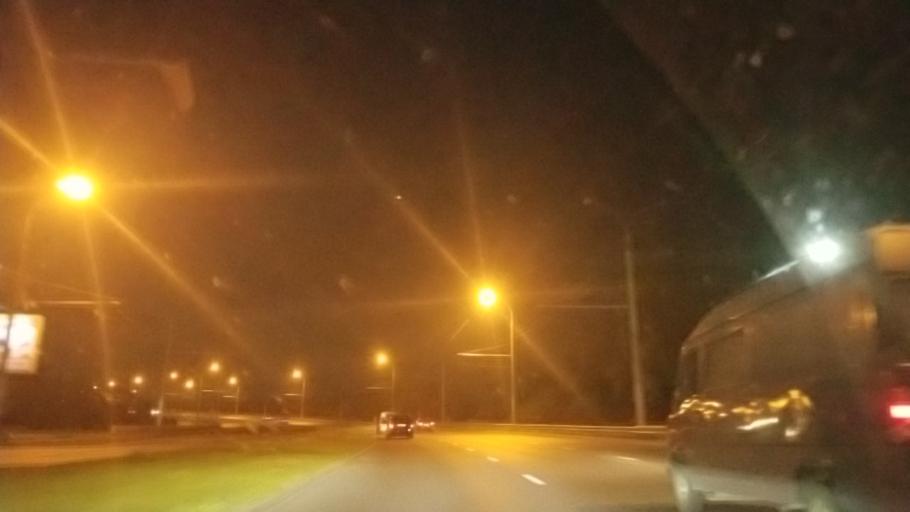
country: BY
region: Brest
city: Brest
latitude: 52.0858
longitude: 23.7726
